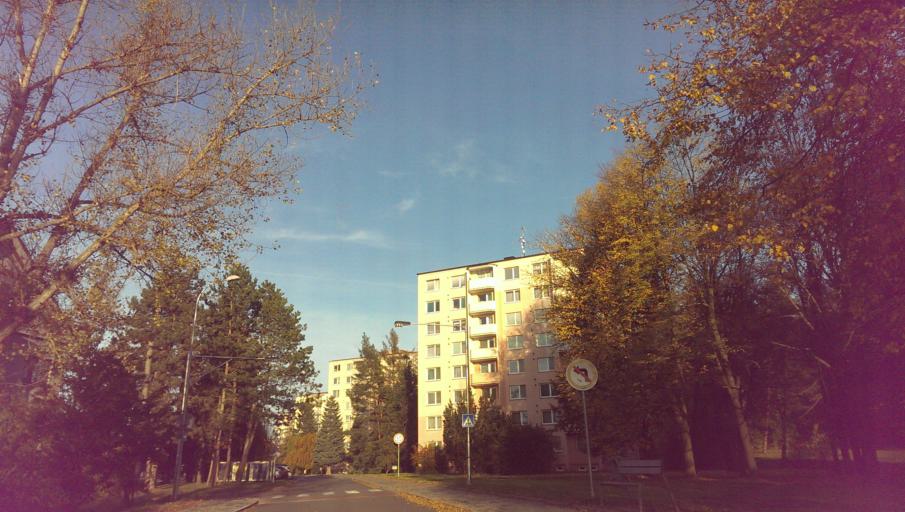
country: CZ
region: Zlin
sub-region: Okres Uherske Hradiste
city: Uherske Hradiste
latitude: 49.0635
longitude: 17.4712
